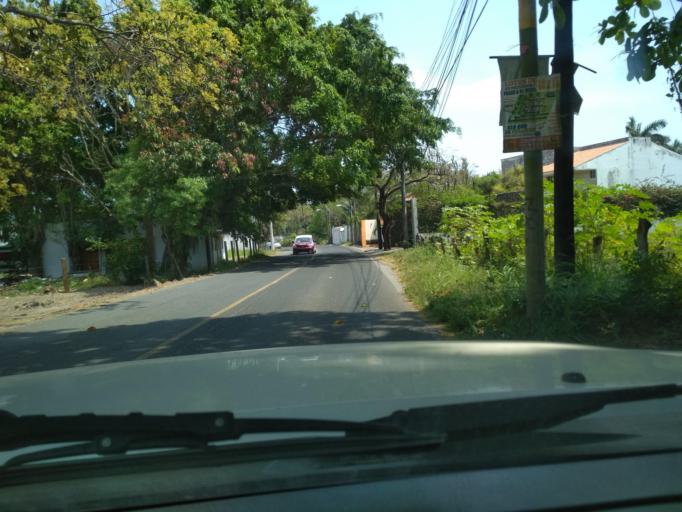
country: MX
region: Veracruz
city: Boca del Rio
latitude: 19.0962
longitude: -96.1274
